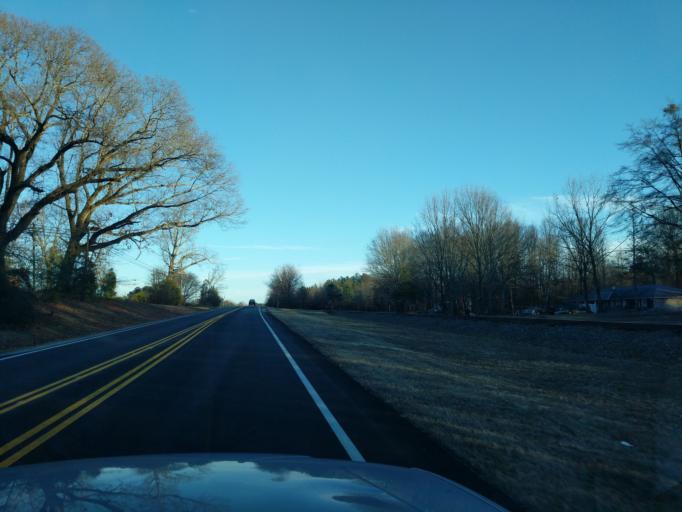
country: US
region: Georgia
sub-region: Franklin County
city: Gumlog
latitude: 34.5093
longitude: -83.2148
